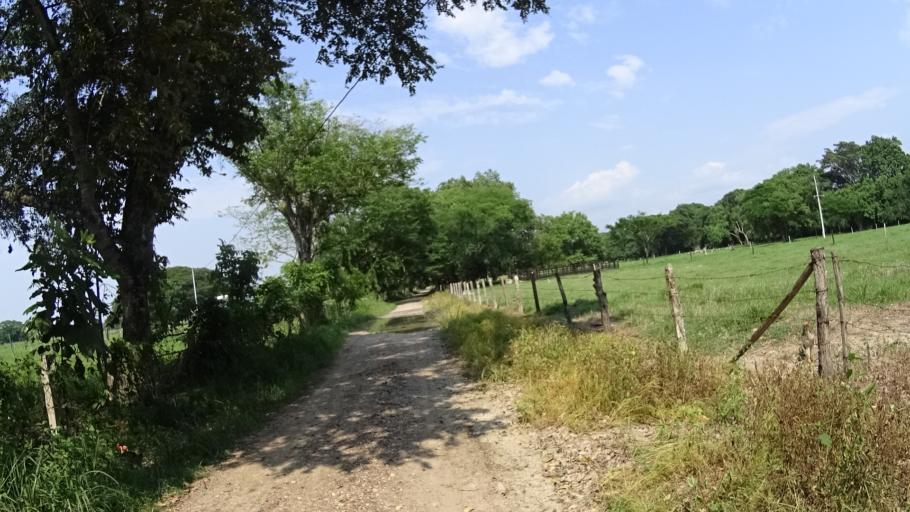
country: CO
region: Cundinamarca
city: Puerto Salgar
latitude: 5.5416
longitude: -74.6733
